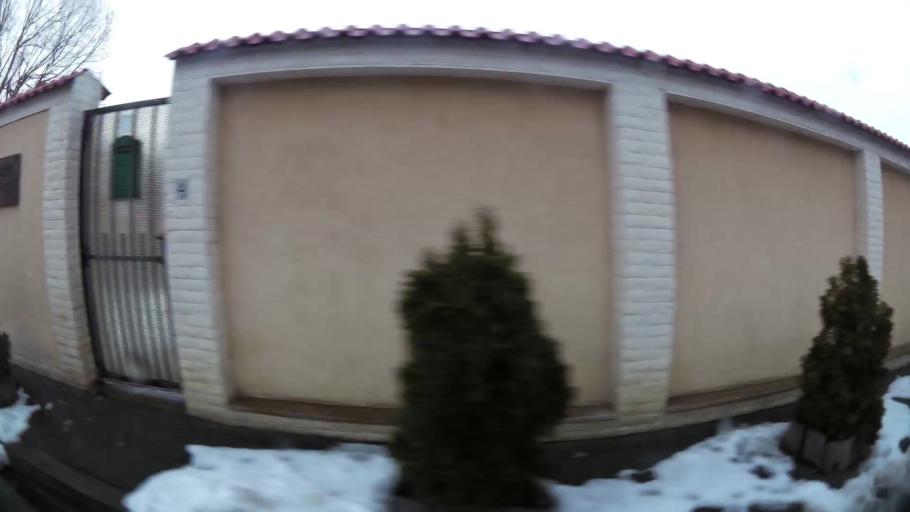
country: RO
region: Ilfov
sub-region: Comuna Mogosoaia
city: Mogosoaia
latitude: 44.5146
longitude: 26.0249
